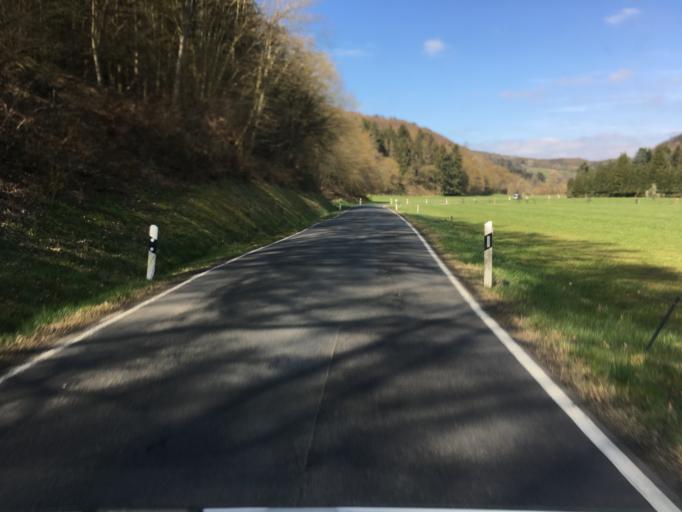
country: DE
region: Rheinland-Pfalz
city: Lind
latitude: 50.5073
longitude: 6.9200
